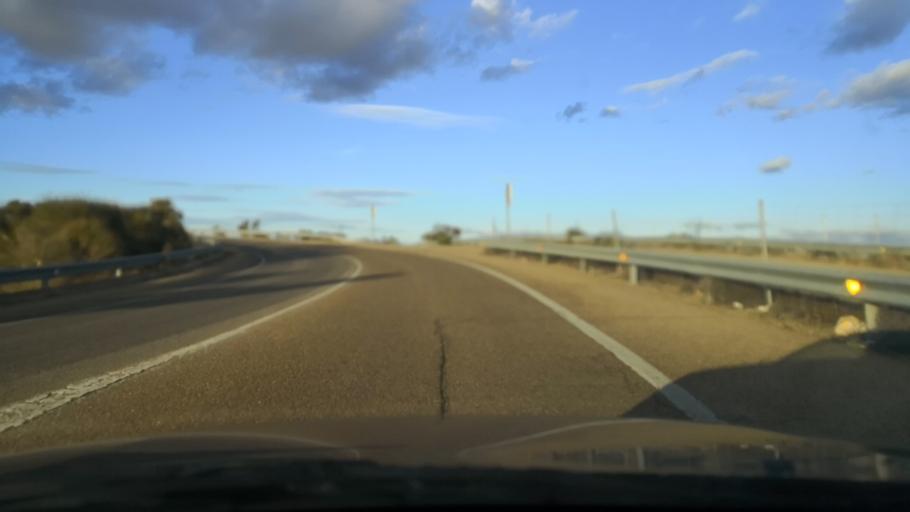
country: ES
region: Castille and Leon
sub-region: Provincia de Valladolid
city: Medina del Campo
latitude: 41.2930
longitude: -4.9000
